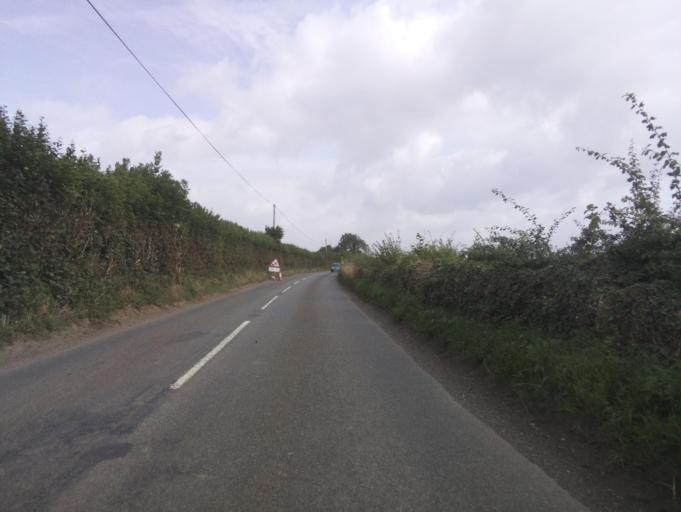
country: GB
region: England
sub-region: Somerset
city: Redlynch
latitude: 51.0844
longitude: -2.4136
